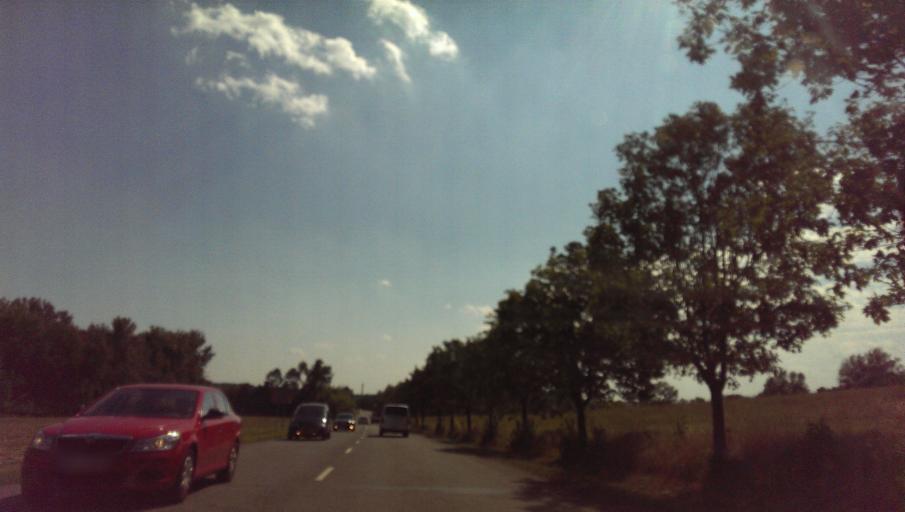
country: CZ
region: Zlin
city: Prusinovice
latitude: 49.3529
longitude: 17.6091
